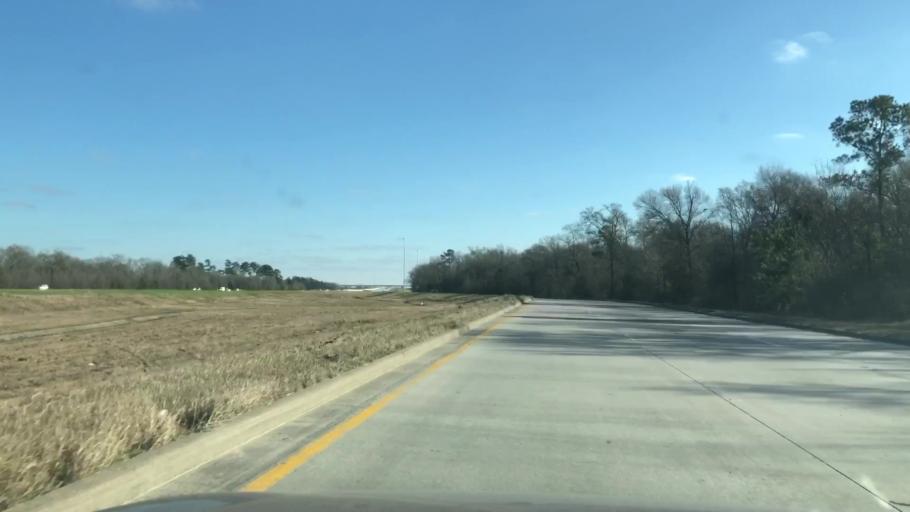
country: US
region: Texas
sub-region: Harris County
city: Cloverleaf
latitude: 29.8232
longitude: -95.1956
